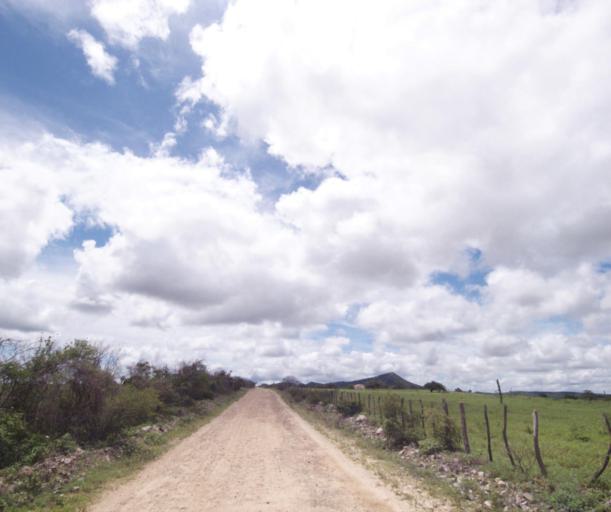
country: BR
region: Bahia
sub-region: Tanhacu
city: Tanhacu
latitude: -14.1759
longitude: -41.1297
